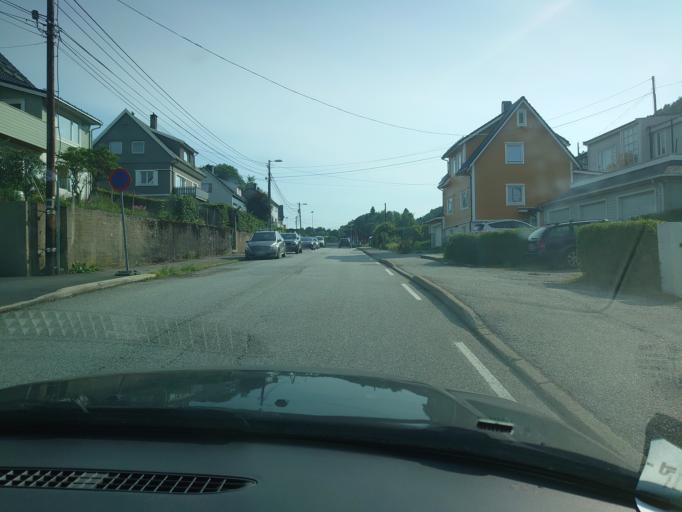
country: NO
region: Hordaland
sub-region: Bergen
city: Bergen
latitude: 60.3728
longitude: 5.3028
